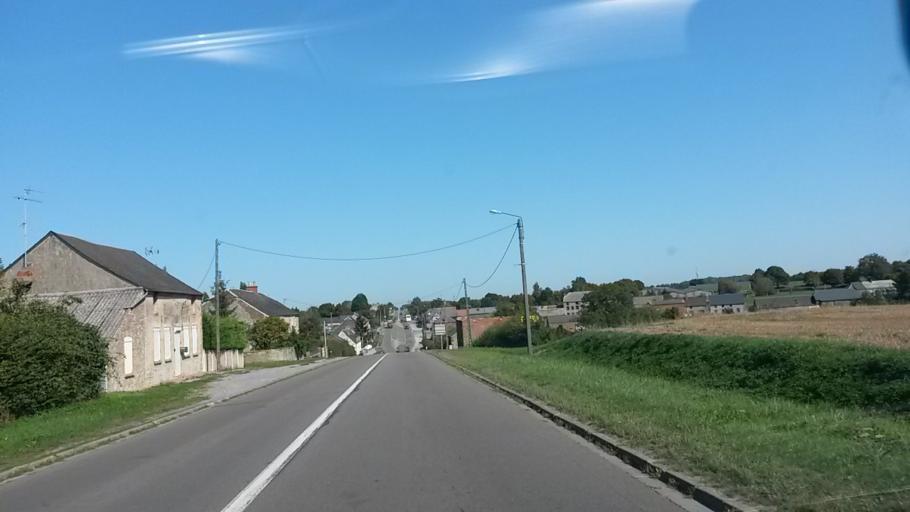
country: FR
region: Nord-Pas-de-Calais
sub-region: Departement du Nord
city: Avesnelles
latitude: 50.1725
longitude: 3.9532
